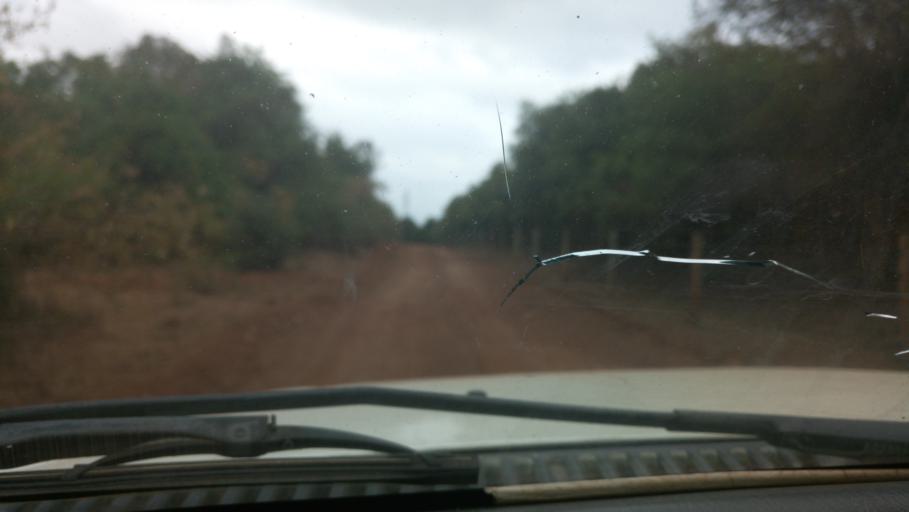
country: KE
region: Nairobi Area
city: Nairobi
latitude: -1.3682
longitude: 36.7680
